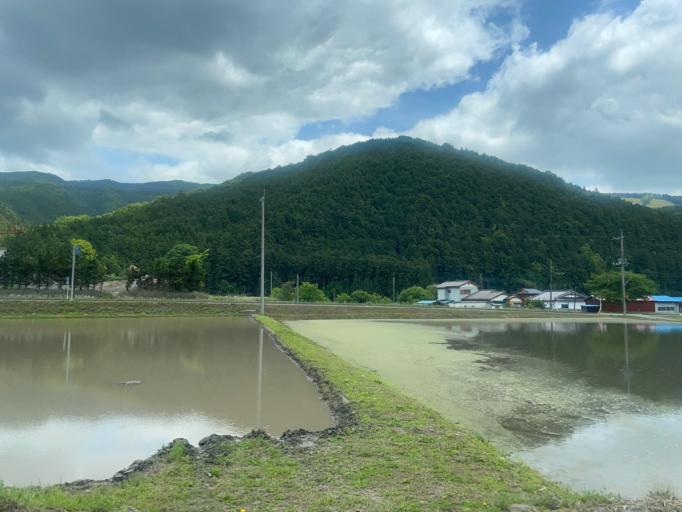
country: JP
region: Tochigi
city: Tanuma
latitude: 36.4651
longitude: 139.6353
